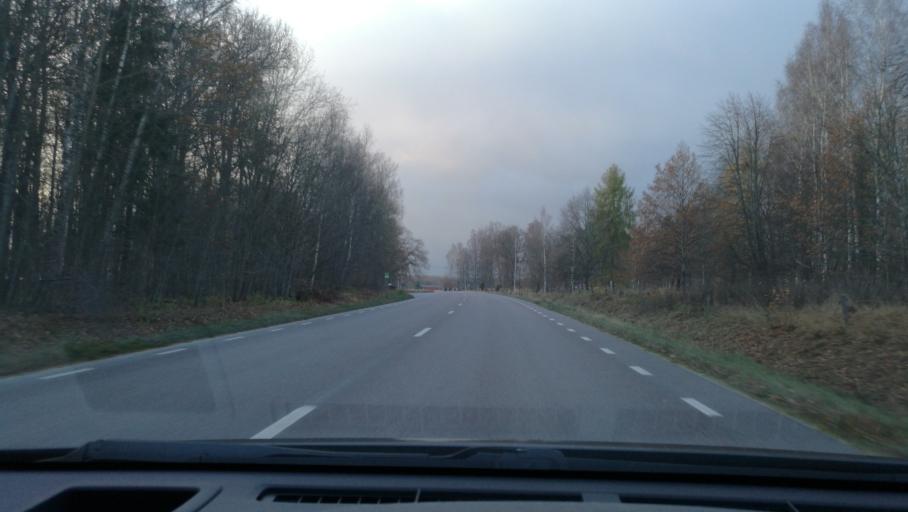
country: SE
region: Soedermanland
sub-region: Vingakers Kommun
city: Vingaker
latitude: 59.1580
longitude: 16.0236
